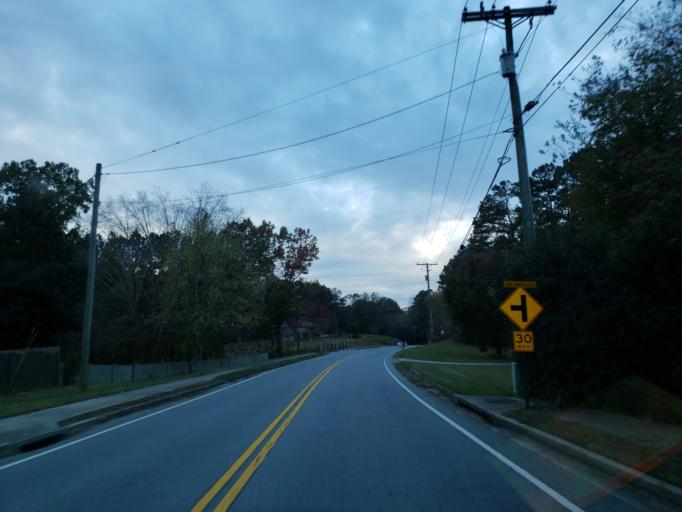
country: US
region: Georgia
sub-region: Cobb County
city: Kennesaw
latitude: 34.0181
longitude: -84.6594
